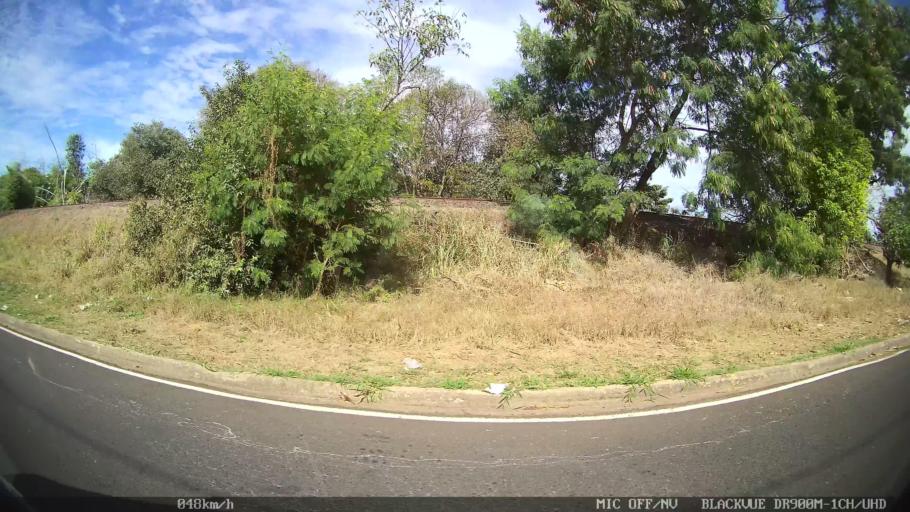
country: BR
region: Sao Paulo
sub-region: Catanduva
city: Catanduva
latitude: -21.1399
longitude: -48.9563
